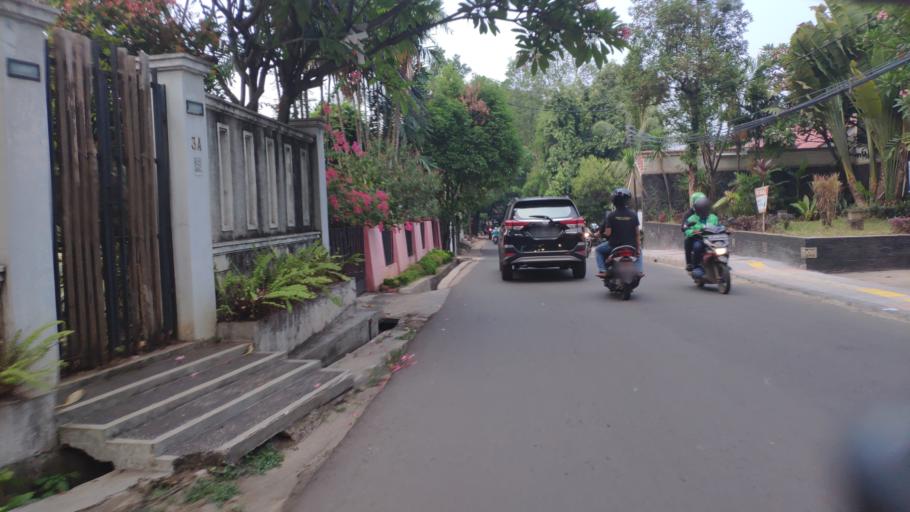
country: ID
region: West Java
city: Pamulang
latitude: -6.3030
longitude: 106.7980
